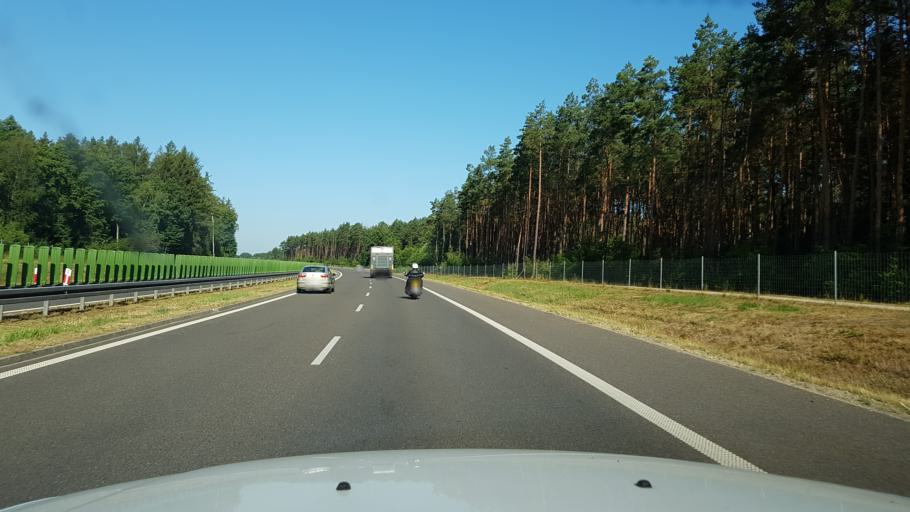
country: PL
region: West Pomeranian Voivodeship
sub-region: Powiat goleniowski
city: Przybiernow
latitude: 53.8412
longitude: 14.7359
